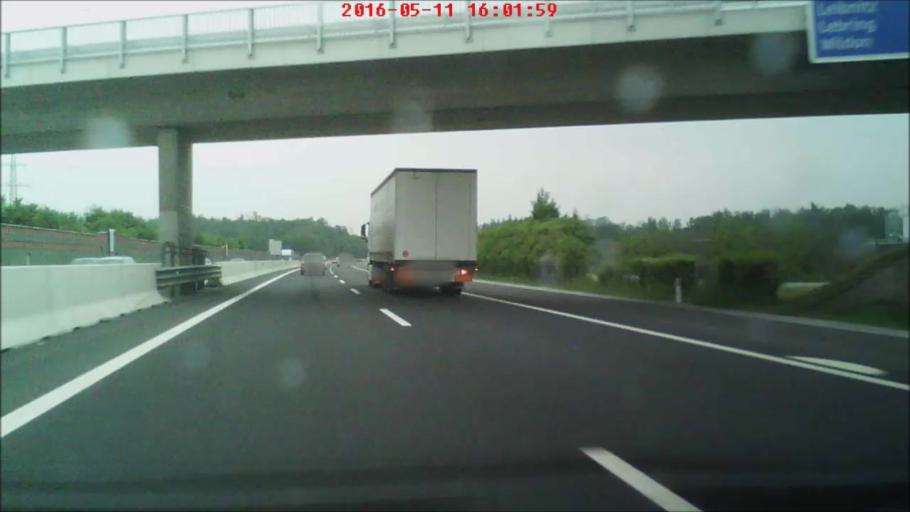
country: AT
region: Styria
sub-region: Politischer Bezirk Graz-Umgebung
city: Wundschuh
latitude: 46.9233
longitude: 15.4687
